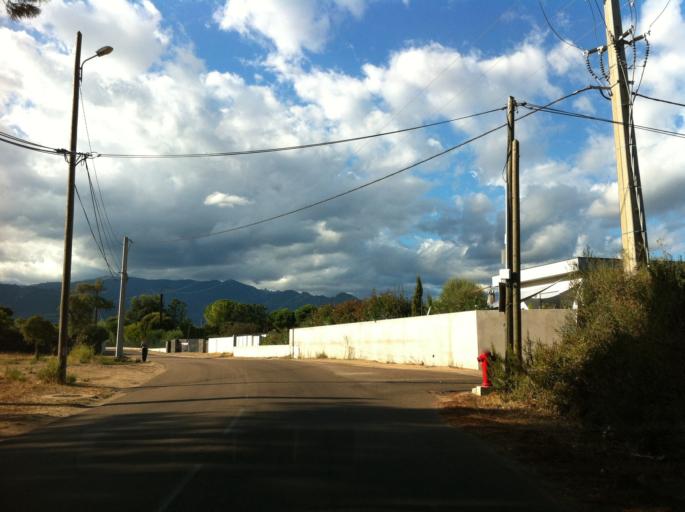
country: FR
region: Corsica
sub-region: Departement de la Corse-du-Sud
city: Porto-Vecchio
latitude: 41.6416
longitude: 9.3329
